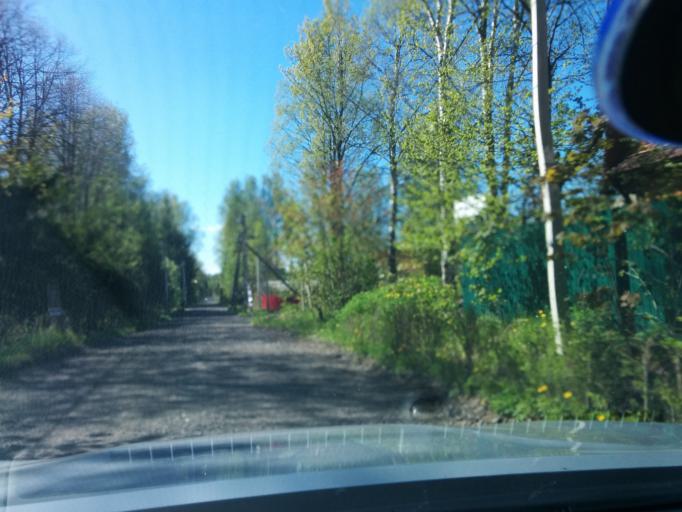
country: RU
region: Leningrad
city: Verkhniye Osel'ki
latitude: 60.2587
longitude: 30.4230
